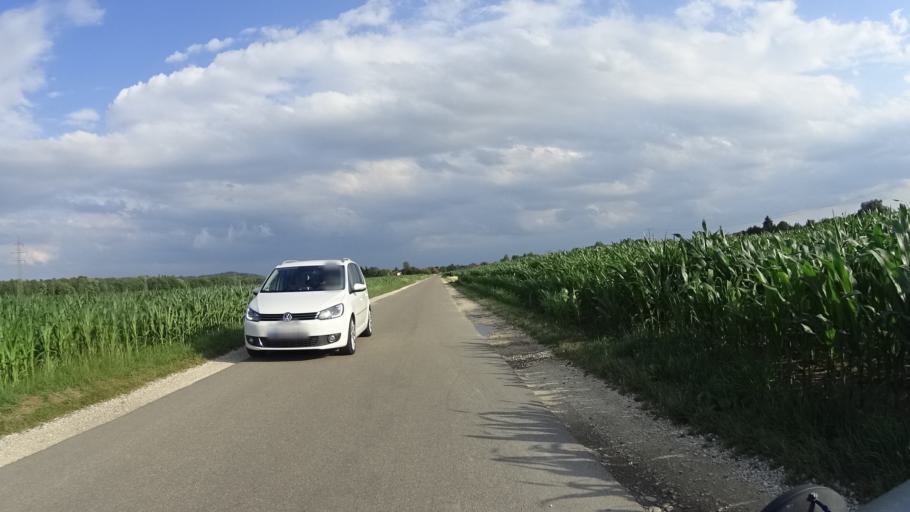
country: DE
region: Bavaria
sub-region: Swabia
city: Altenstadt
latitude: 48.1545
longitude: 10.0953
